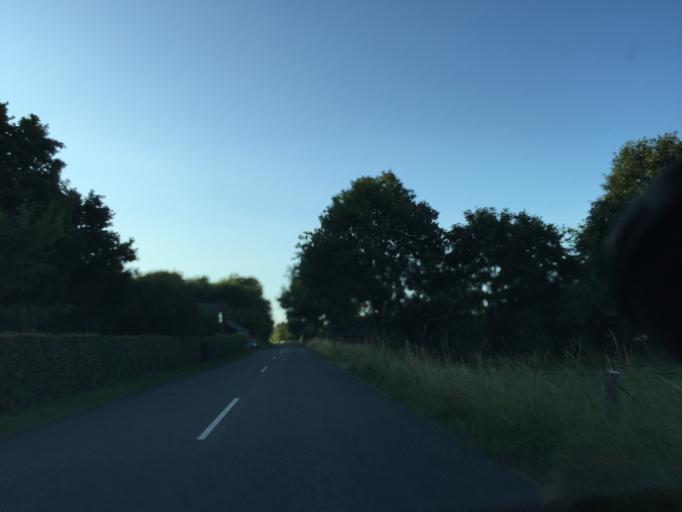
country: DK
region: Central Jutland
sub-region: Silkeborg Kommune
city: Svejbaek
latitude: 56.2284
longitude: 9.6656
